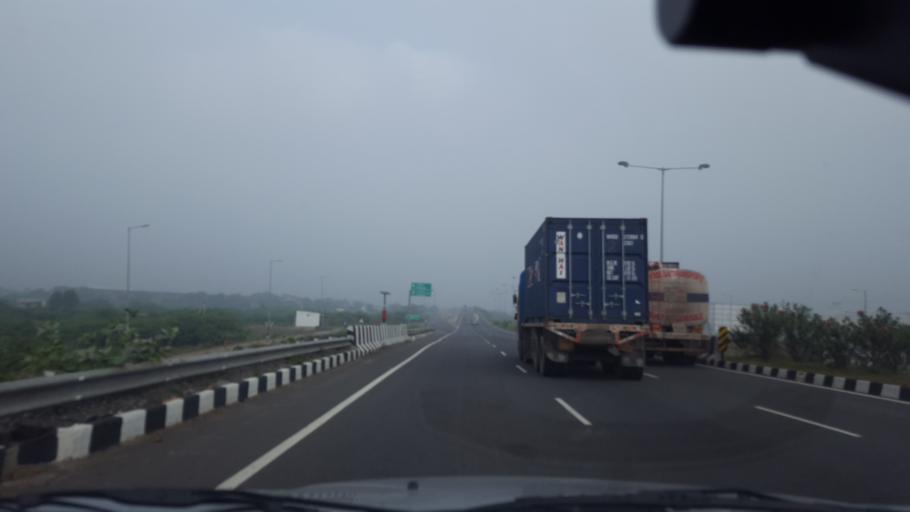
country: IN
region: Andhra Pradesh
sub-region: Prakasam
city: Ongole
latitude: 15.5286
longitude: 80.0566
